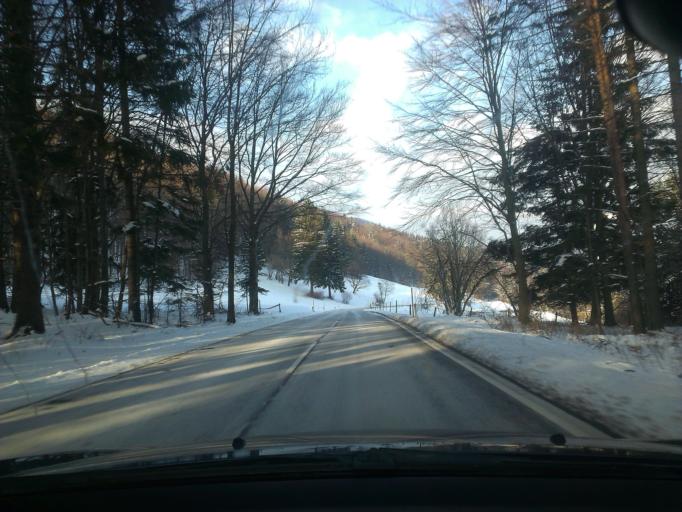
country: AT
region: Lower Austria
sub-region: Politischer Bezirk Neunkirchen
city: Puchberg am Schneeberg
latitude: 47.8146
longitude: 15.9417
